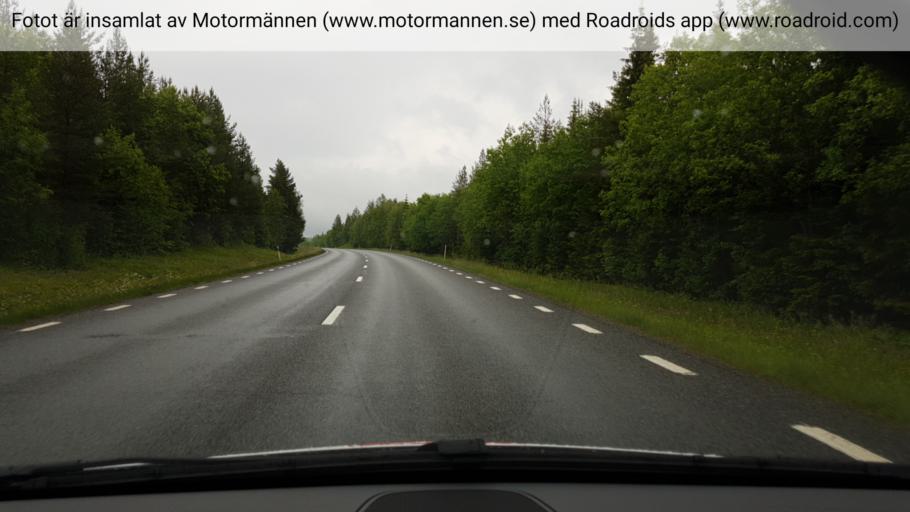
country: SE
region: Jaemtland
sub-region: OEstersunds Kommun
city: Lit
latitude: 63.3977
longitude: 15.0481
